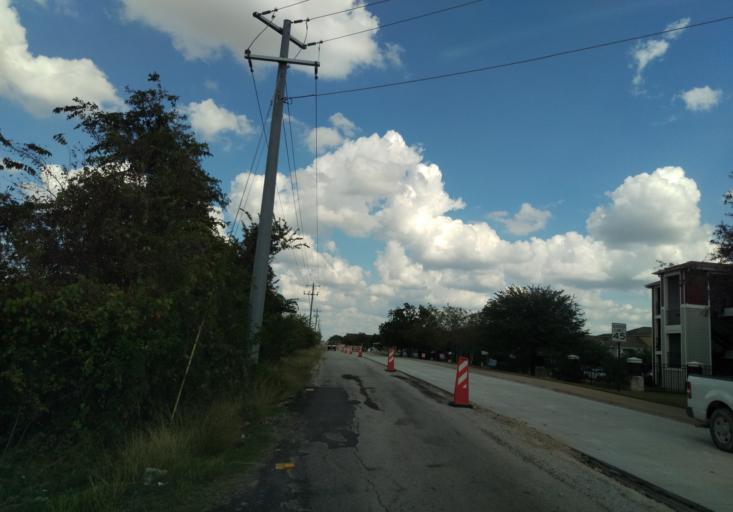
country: US
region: Texas
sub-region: Brazos County
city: College Station
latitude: 30.5886
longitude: -96.3482
